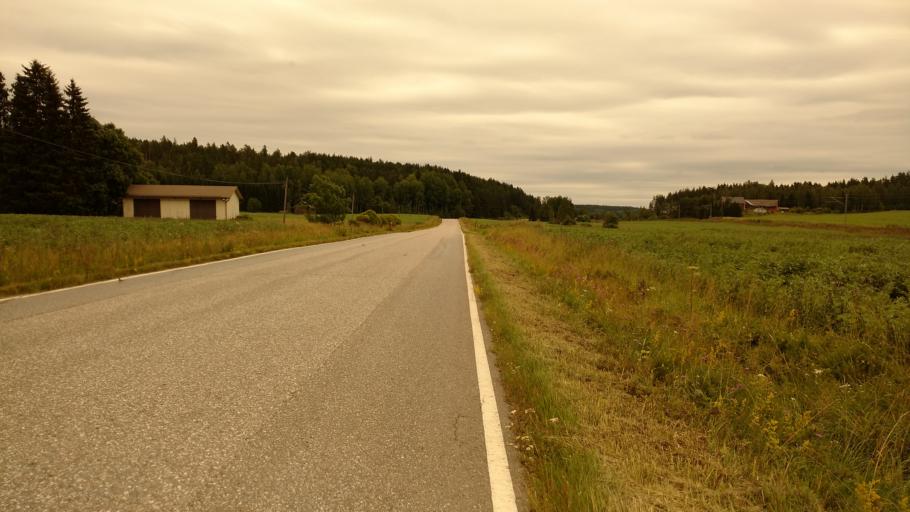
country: FI
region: Varsinais-Suomi
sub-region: Loimaa
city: Marttila
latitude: 60.4163
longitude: 22.8640
